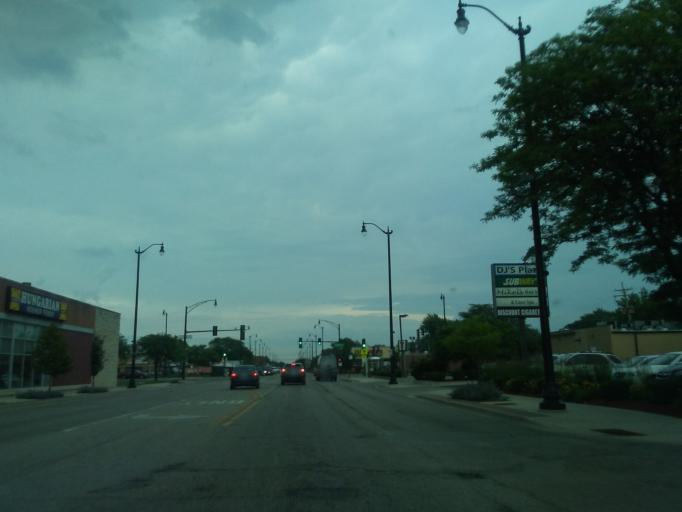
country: US
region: Illinois
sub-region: Cook County
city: Skokie
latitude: 42.0263
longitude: -87.7294
